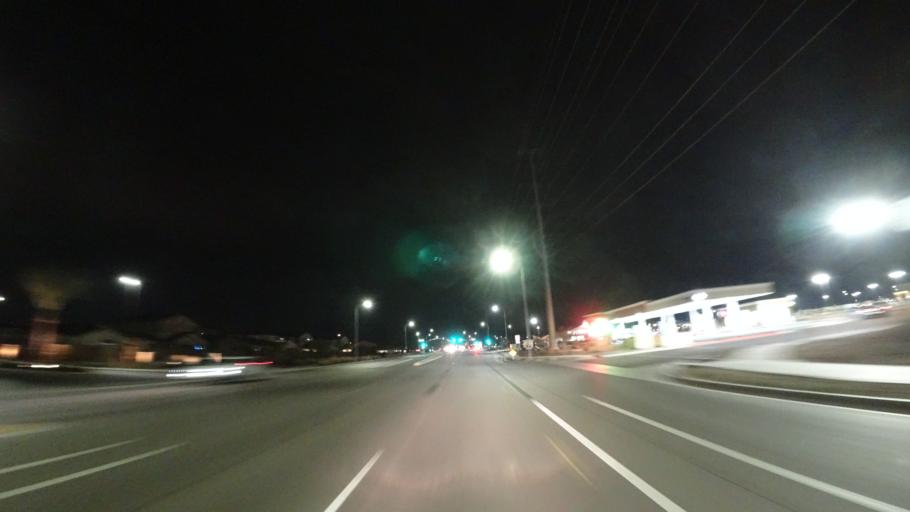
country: US
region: Arizona
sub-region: Maricopa County
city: Chandler
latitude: 33.2482
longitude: -111.7918
